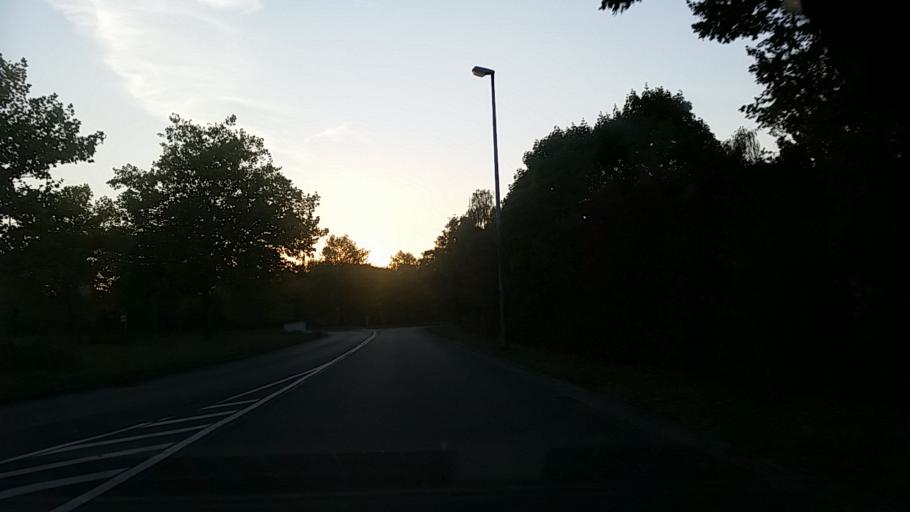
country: DE
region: Lower Saxony
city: Wolfsburg
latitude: 52.4000
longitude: 10.7501
